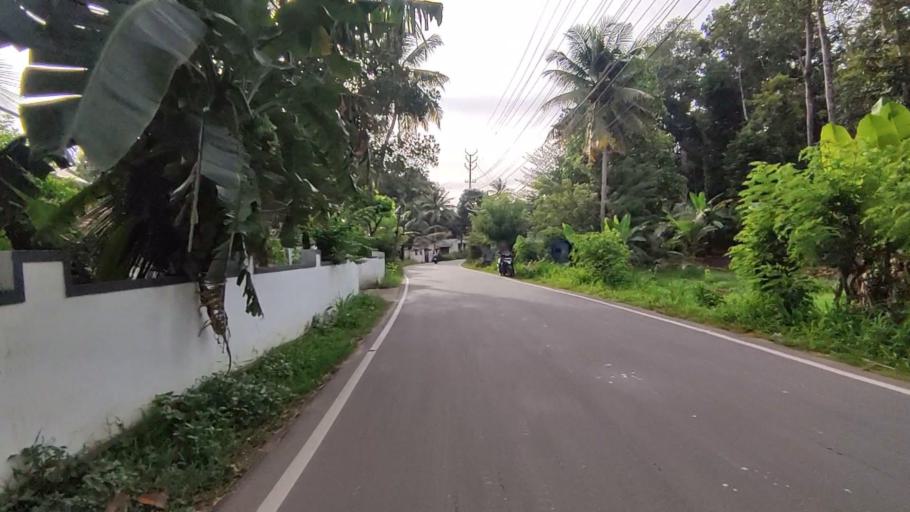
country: IN
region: Kerala
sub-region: Kottayam
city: Kottayam
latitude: 9.6021
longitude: 76.5034
